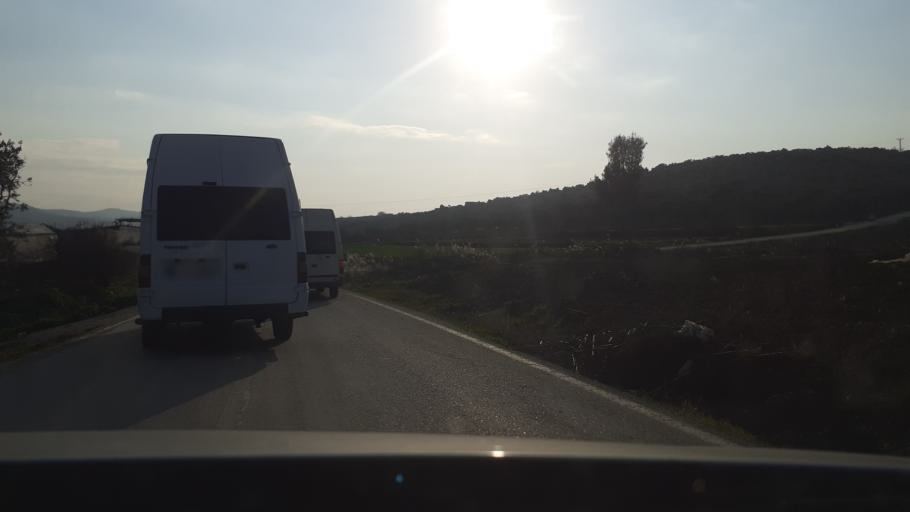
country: TR
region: Hatay
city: Boynuyogun
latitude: 36.1401
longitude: 36.3165
